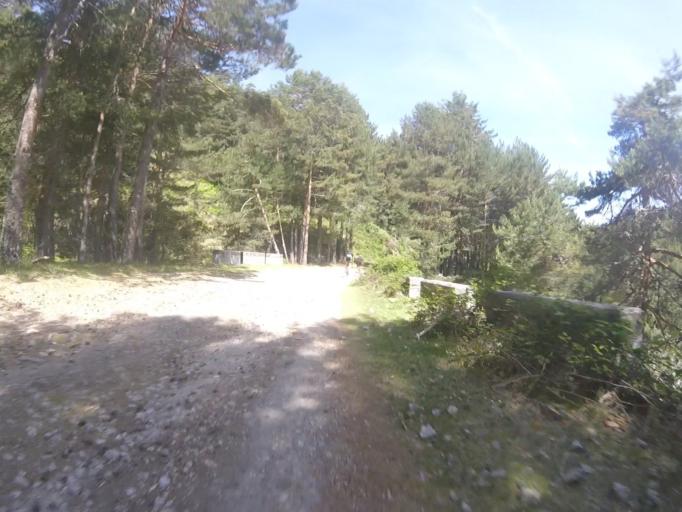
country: ES
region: Madrid
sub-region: Provincia de Madrid
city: Cercedilla
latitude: 40.8095
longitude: -4.0562
